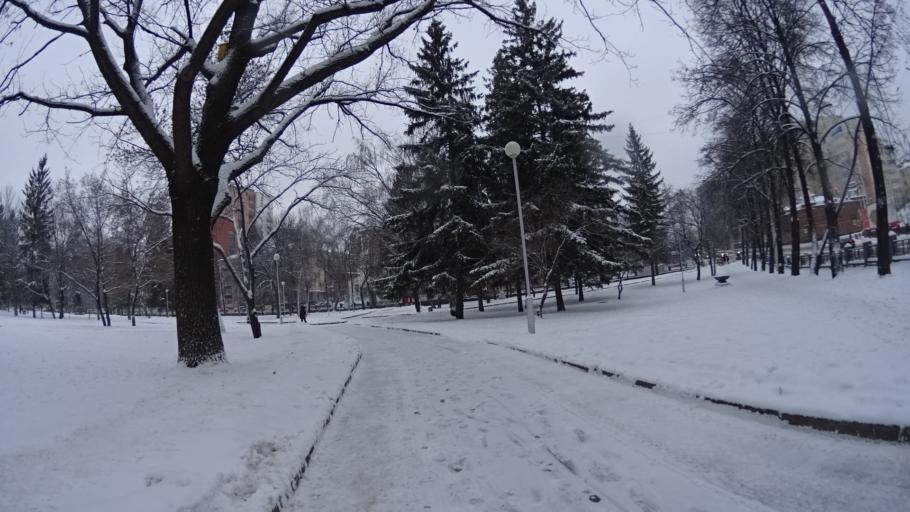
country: RU
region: Bashkortostan
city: Ufa
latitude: 54.7246
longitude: 55.9522
